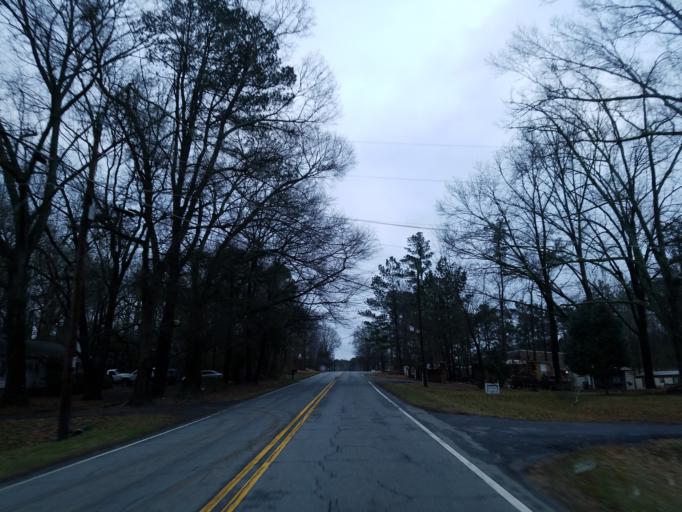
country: US
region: Georgia
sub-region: Cobb County
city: Acworth
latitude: 34.0831
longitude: -84.6973
